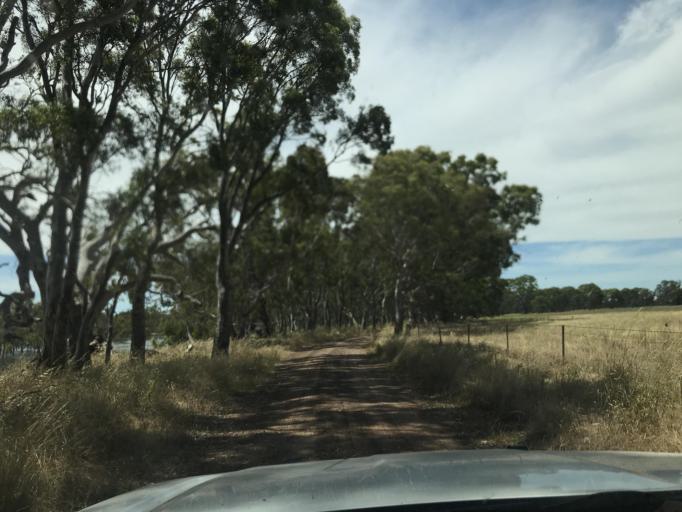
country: AU
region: South Australia
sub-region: Wattle Range
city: Penola
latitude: -37.0008
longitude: 141.4950
